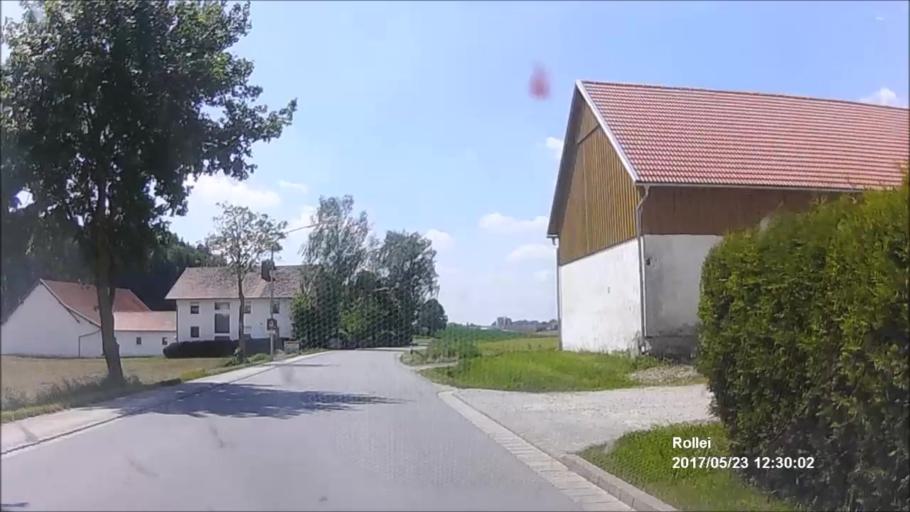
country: DE
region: Bavaria
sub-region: Lower Bavaria
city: Buch
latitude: 48.6584
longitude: 12.1343
